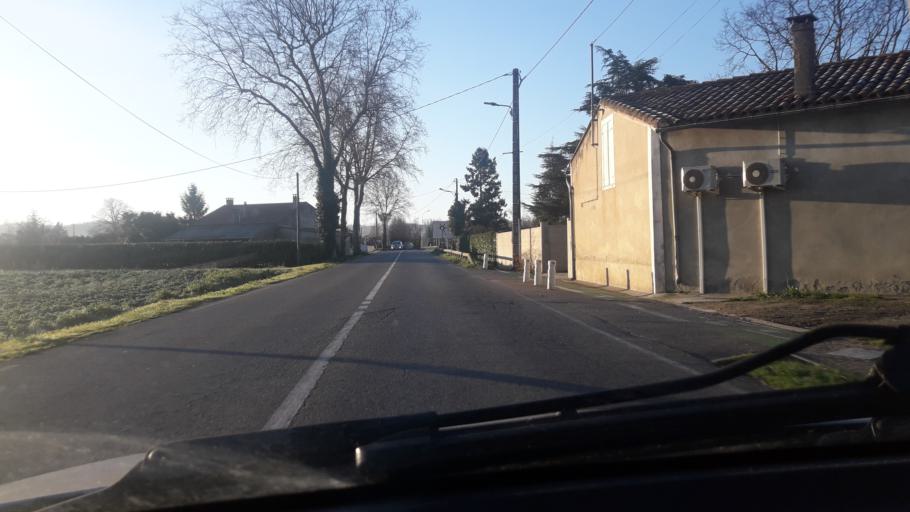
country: FR
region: Midi-Pyrenees
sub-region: Departement de la Haute-Garonne
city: Carbonne
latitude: 43.3123
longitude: 1.2221
